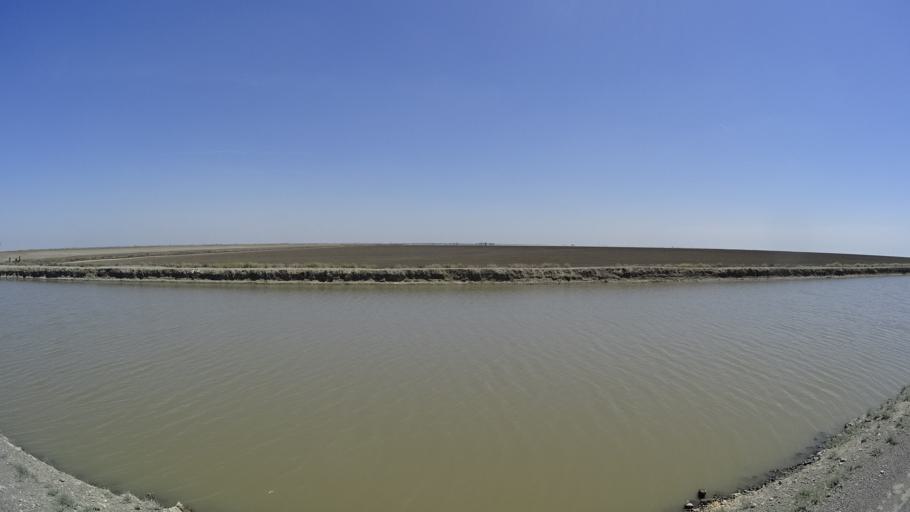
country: US
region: California
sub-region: Kings County
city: Corcoran
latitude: 36.0408
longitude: -119.6435
